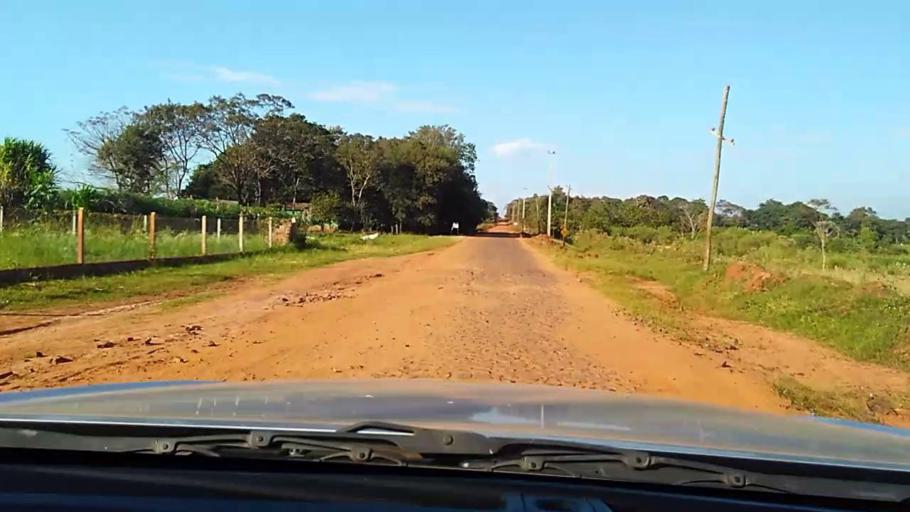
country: PY
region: Alto Parana
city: Doctor Juan Leon Mallorquin
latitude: -25.6848
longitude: -55.3763
